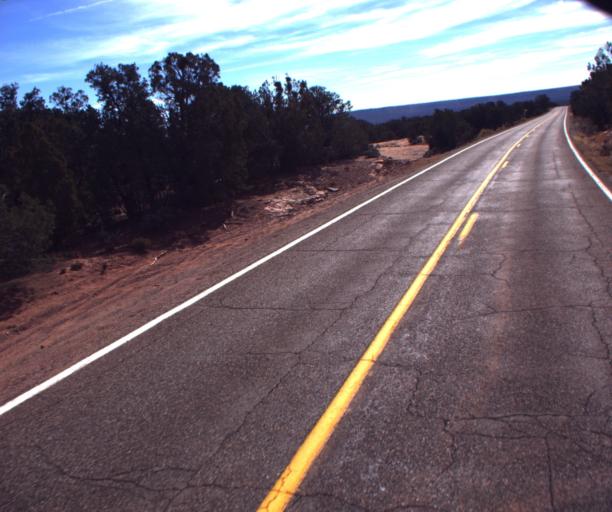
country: US
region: Arizona
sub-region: Navajo County
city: Kayenta
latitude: 36.6371
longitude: -110.5103
